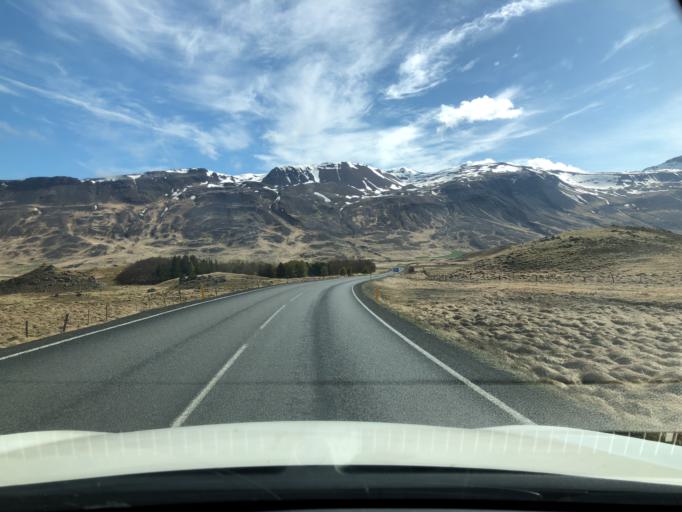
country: IS
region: Northwest
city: Saudarkrokur
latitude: 65.5045
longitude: -20.3839
